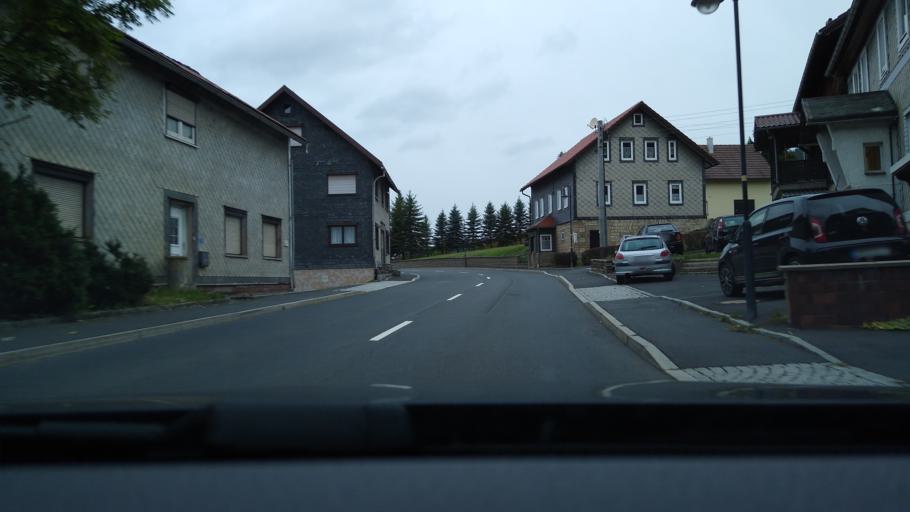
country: DE
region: Thuringia
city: Bachfeld
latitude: 50.4503
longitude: 10.9717
